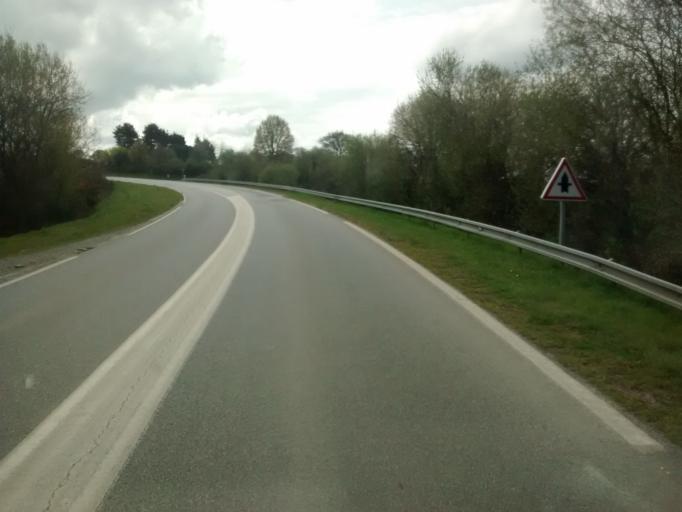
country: FR
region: Brittany
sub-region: Departement du Morbihan
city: Ploermel
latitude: 47.9136
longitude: -2.3891
